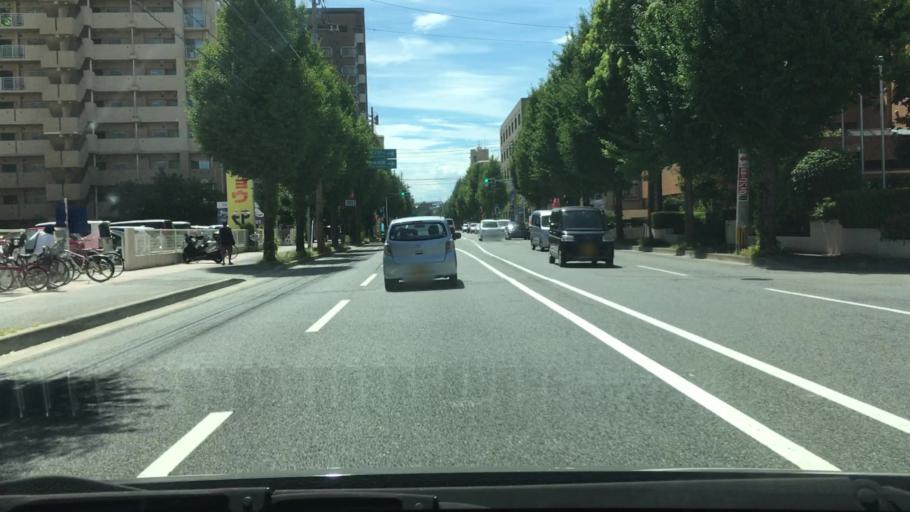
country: JP
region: Fukuoka
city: Fukuoka-shi
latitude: 33.5688
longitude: 130.4256
